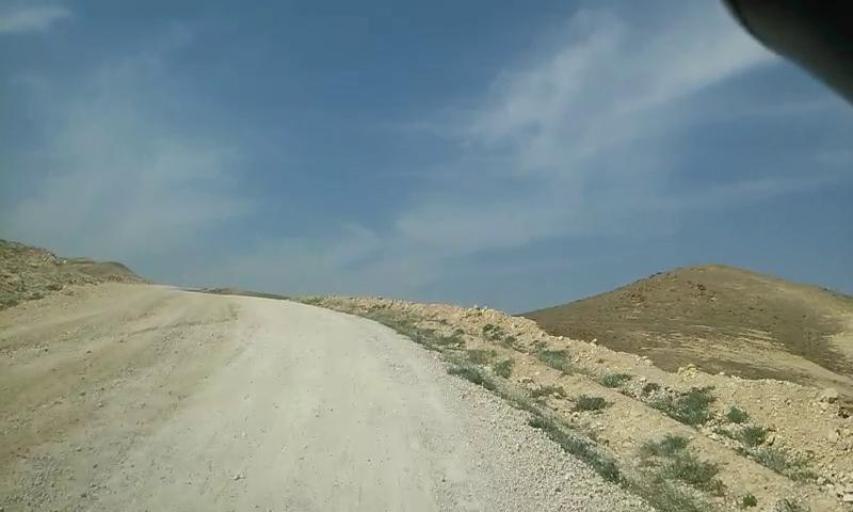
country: PS
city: `Arab ar Rashaydah
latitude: 31.4844
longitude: 35.2770
